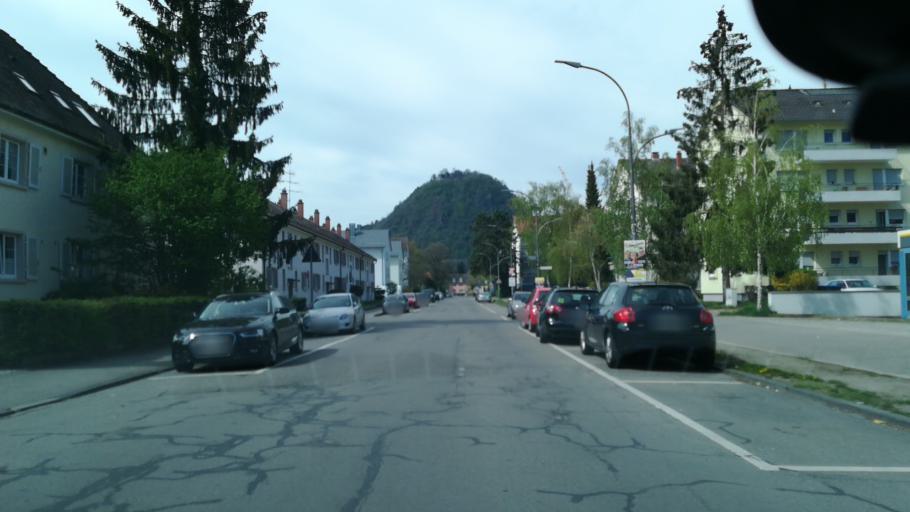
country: DE
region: Baden-Wuerttemberg
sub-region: Freiburg Region
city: Singen
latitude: 47.7685
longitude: 8.8379
